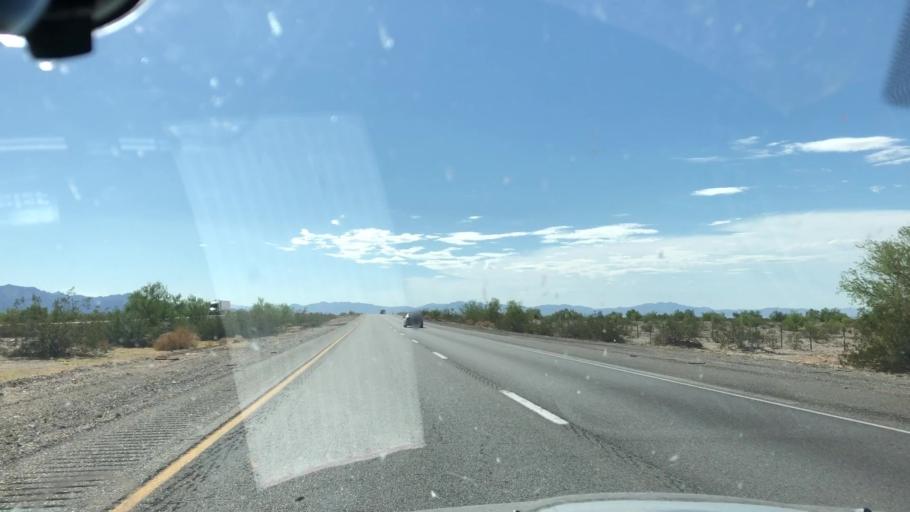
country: US
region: California
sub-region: Riverside County
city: Mesa Verde
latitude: 33.6611
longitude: -115.1706
